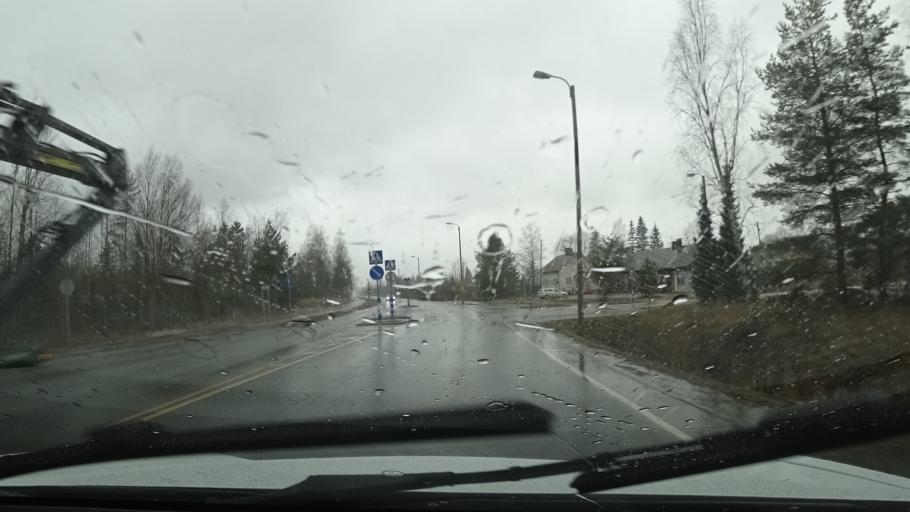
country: FI
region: Paijanne Tavastia
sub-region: Lahti
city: Orimattila
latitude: 60.8027
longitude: 25.7651
